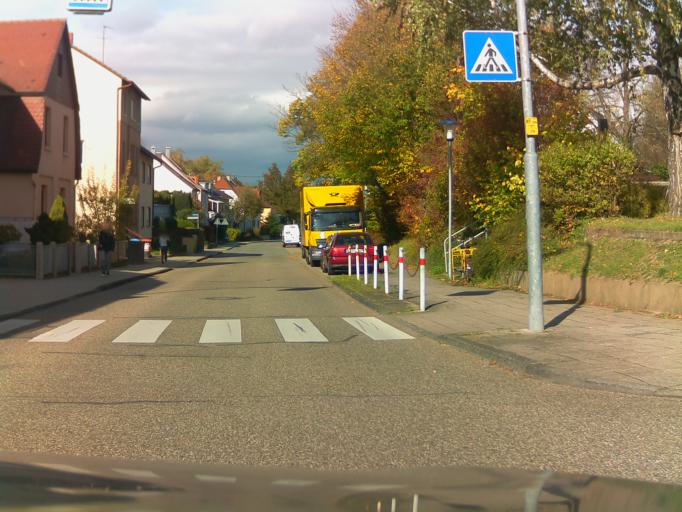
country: DE
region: Baden-Wuerttemberg
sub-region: Karlsruhe Region
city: Weingarten
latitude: 49.0109
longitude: 8.4950
